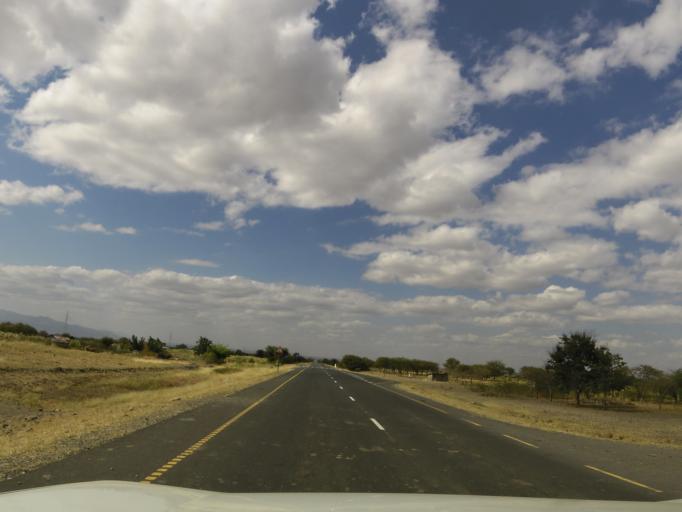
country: TZ
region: Arusha
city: Mto wa Mbu
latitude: -3.6326
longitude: 36.0115
